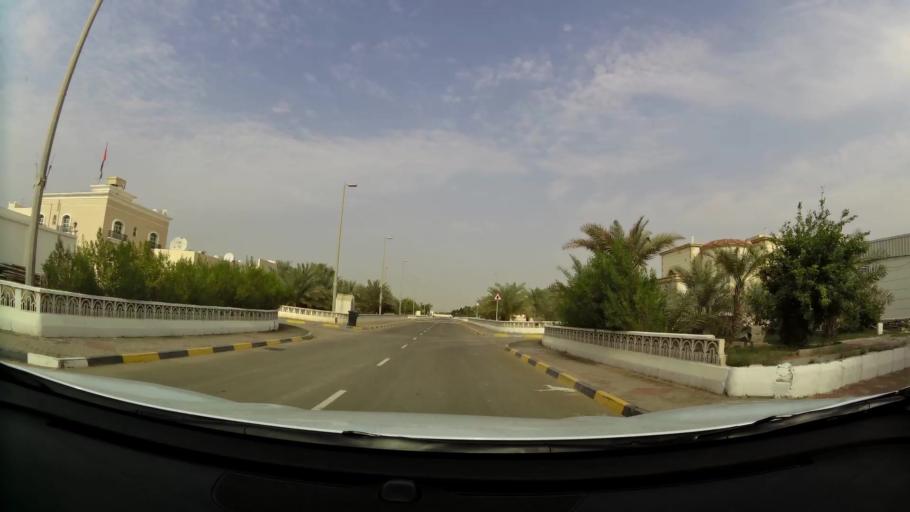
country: AE
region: Abu Dhabi
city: Abu Dhabi
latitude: 24.6698
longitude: 54.7517
